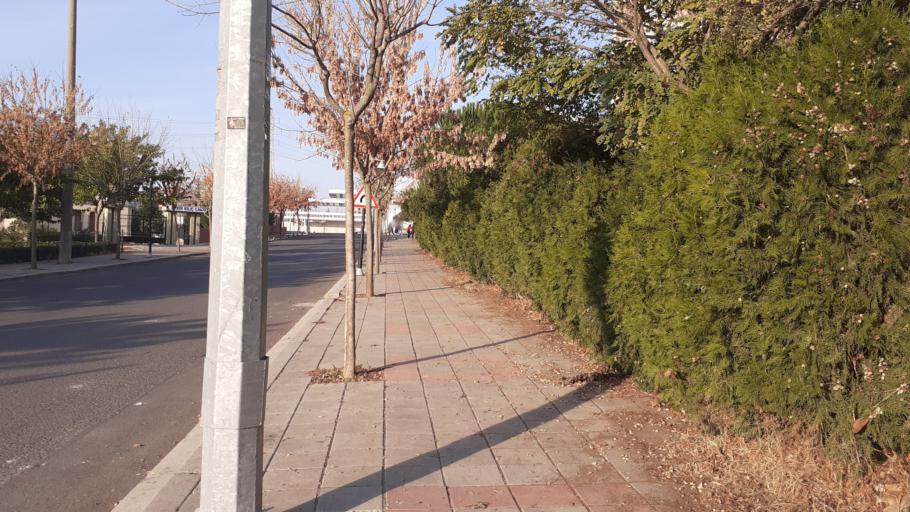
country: TR
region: Tekirdag
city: Corlu
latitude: 41.1470
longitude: 27.8275
